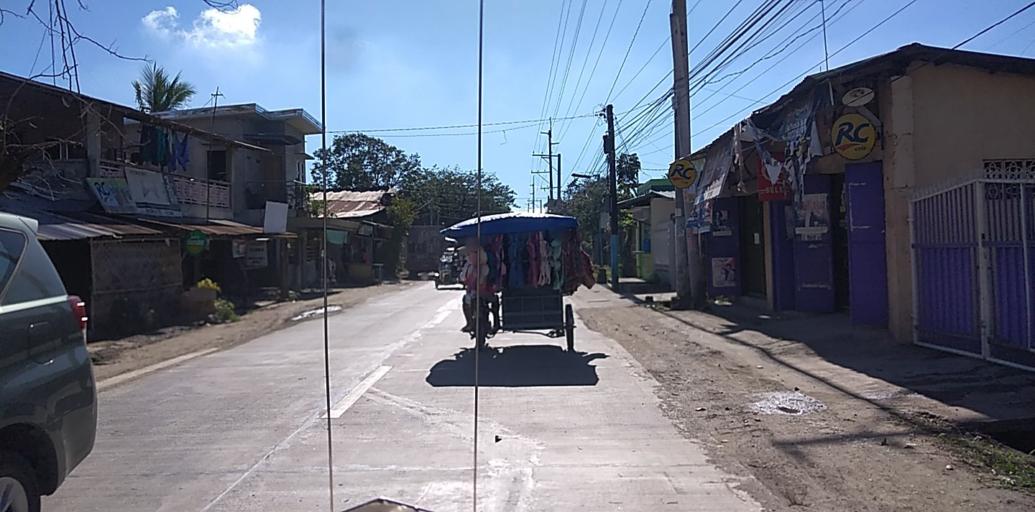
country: PH
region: Central Luzon
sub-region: Province of Pampanga
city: San Luis
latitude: 15.0563
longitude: 120.7769
